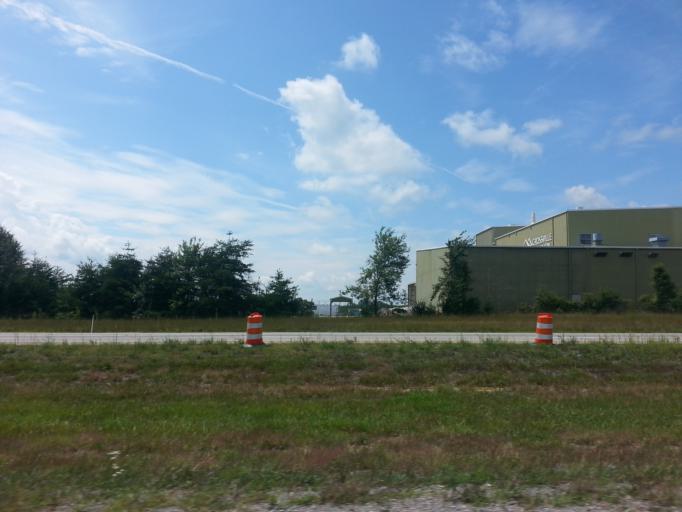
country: US
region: Tennessee
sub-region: Cumberland County
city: Crossville
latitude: 35.9845
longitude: -85.0161
